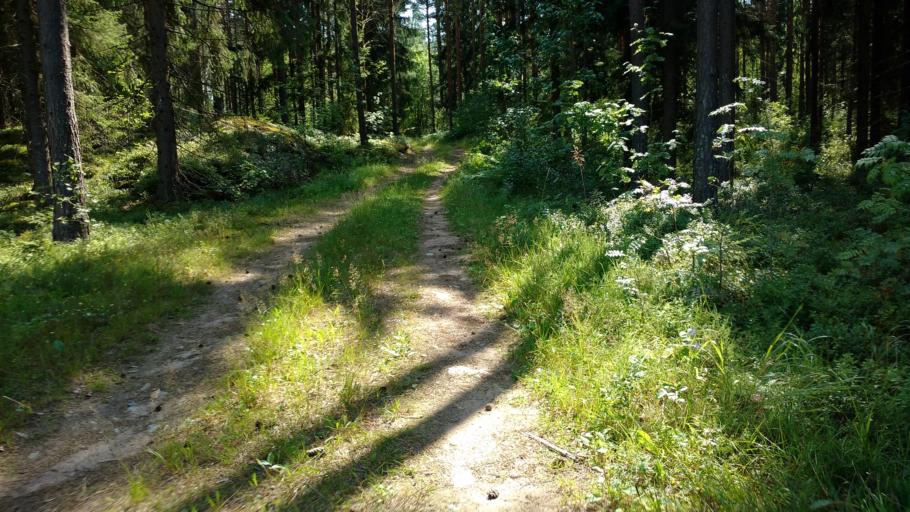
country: FI
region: Varsinais-Suomi
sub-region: Salo
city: Pertteli
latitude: 60.4075
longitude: 23.2030
